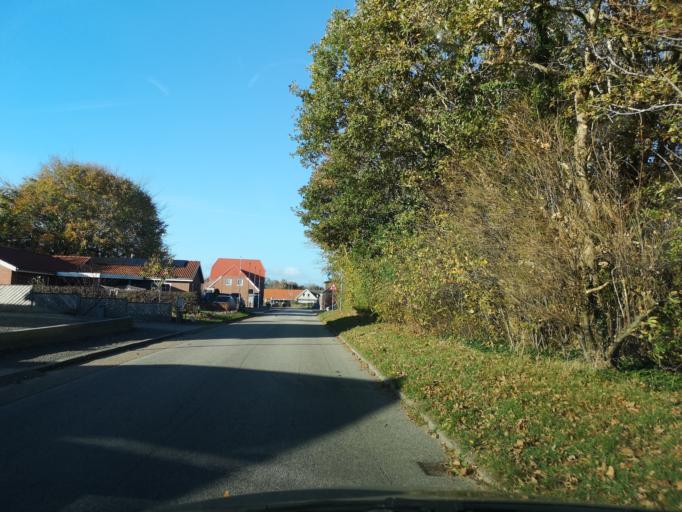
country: DK
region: Central Jutland
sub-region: Ringkobing-Skjern Kommune
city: Tarm
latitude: 55.8209
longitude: 8.4106
